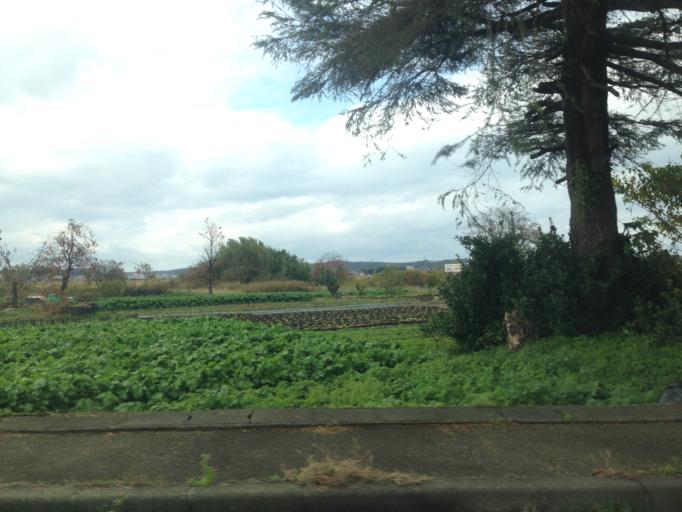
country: JP
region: Ishikawa
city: Komatsu
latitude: 36.3031
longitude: 136.3697
